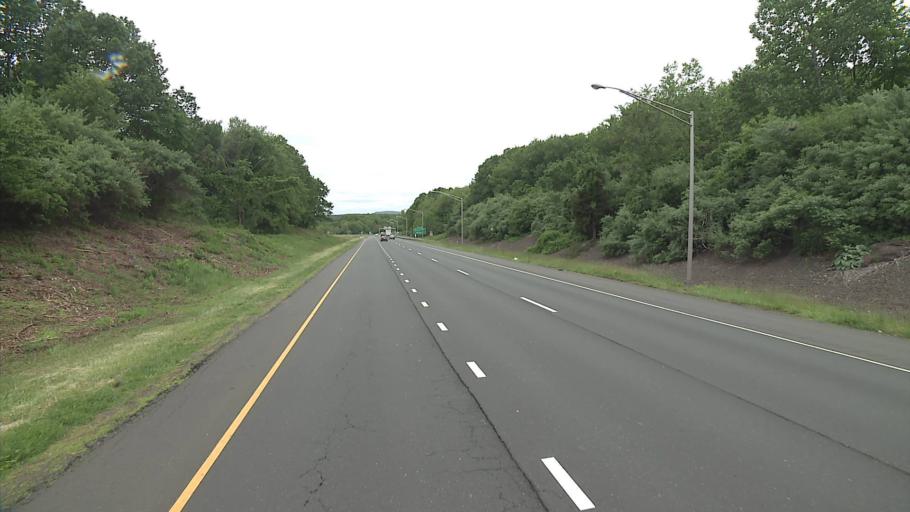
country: US
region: Connecticut
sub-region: Middlesex County
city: Cromwell
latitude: 41.6258
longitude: -72.7019
